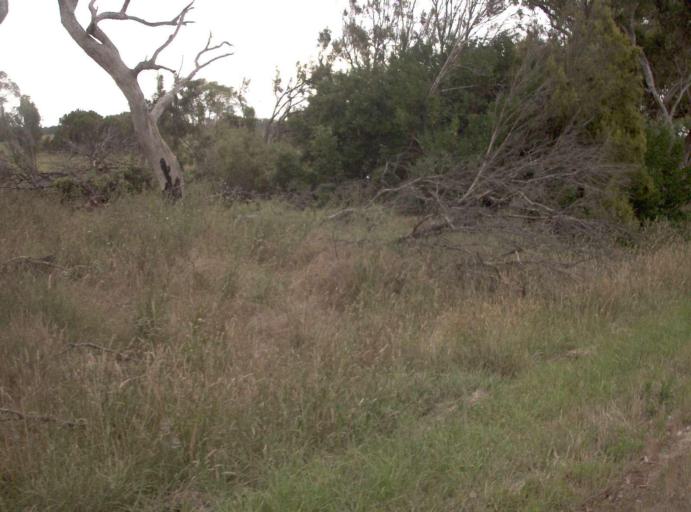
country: AU
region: Victoria
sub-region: Latrobe
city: Traralgon
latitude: -38.5547
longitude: 146.8150
